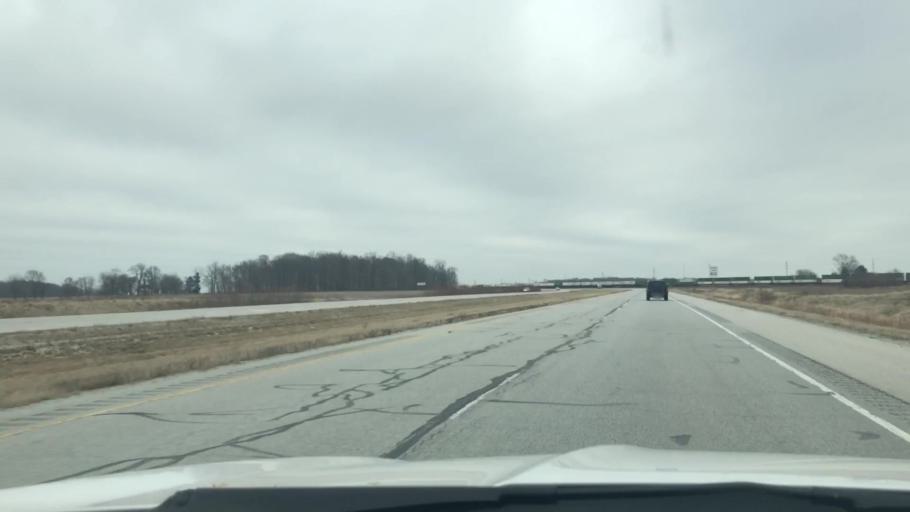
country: US
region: Indiana
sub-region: Cass County
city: Georgetown
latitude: 40.6824
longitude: -86.5051
